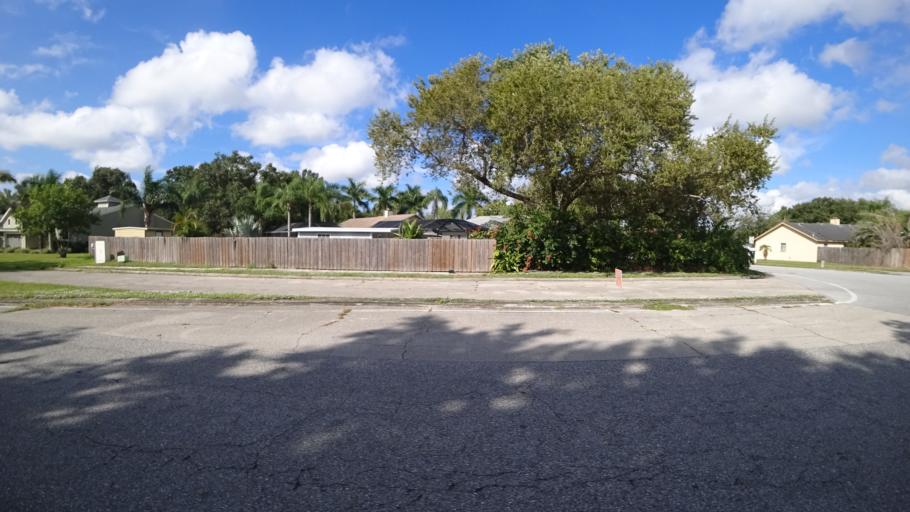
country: US
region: Florida
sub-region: Sarasota County
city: North Sarasota
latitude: 27.4056
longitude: -82.5135
